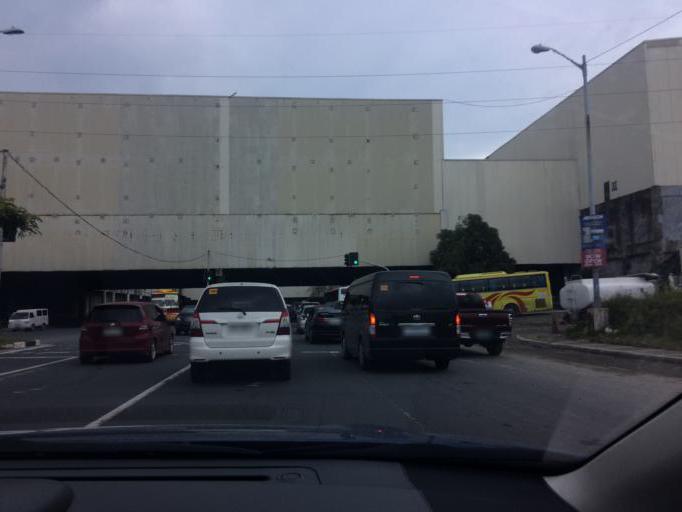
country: PH
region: Metro Manila
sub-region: Makati City
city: Makati City
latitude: 14.5143
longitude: 120.9904
